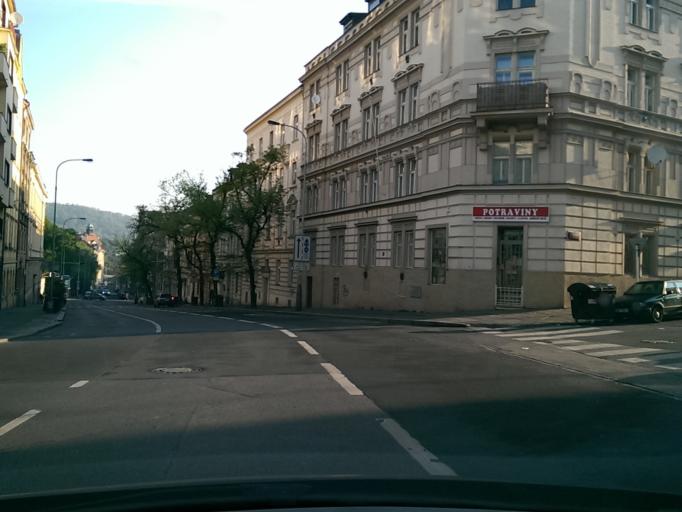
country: CZ
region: Praha
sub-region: Praha 2
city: Vysehrad
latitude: 50.0669
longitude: 14.3994
